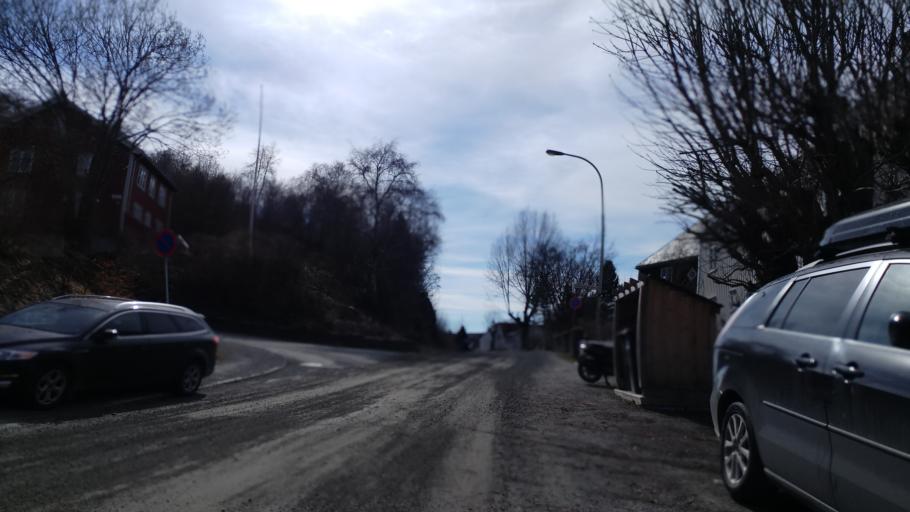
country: NO
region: Sor-Trondelag
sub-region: Trondheim
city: Trondheim
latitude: 63.4321
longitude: 10.4286
